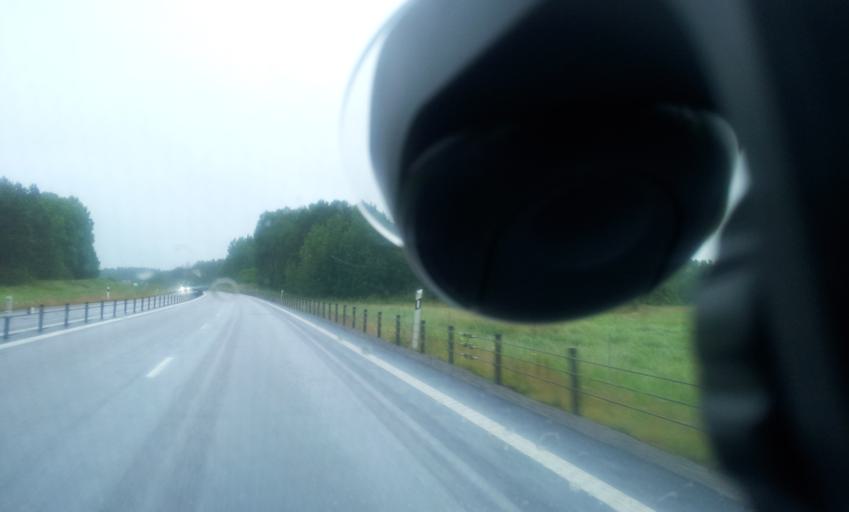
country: SE
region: OEstergoetland
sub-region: Soderkopings Kommun
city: Soederkoeping
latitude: 58.4127
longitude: 16.4008
